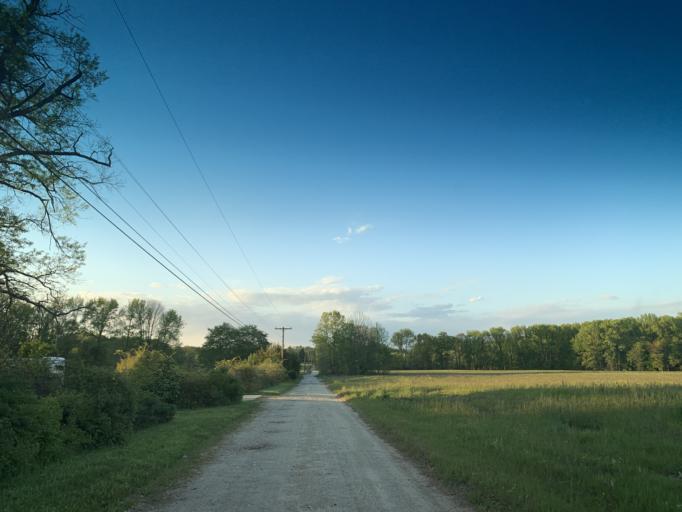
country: US
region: Maryland
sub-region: Harford County
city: Aberdeen
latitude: 39.5072
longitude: -76.1906
